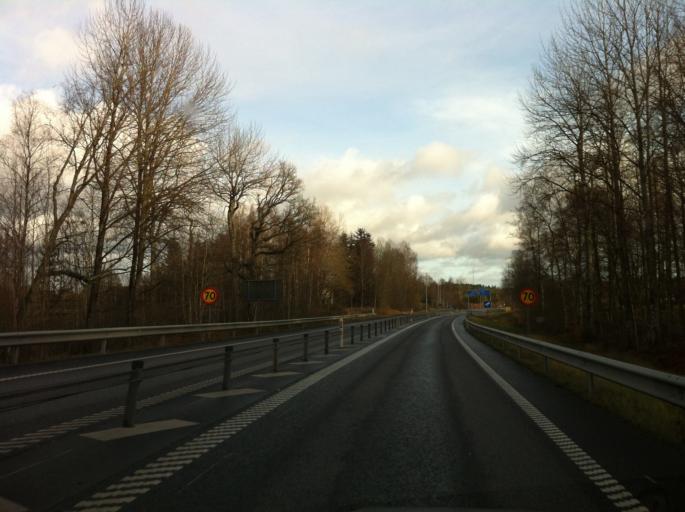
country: SE
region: Kronoberg
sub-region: Alvesta Kommun
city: Vislanda
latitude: 56.7036
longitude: 14.3910
